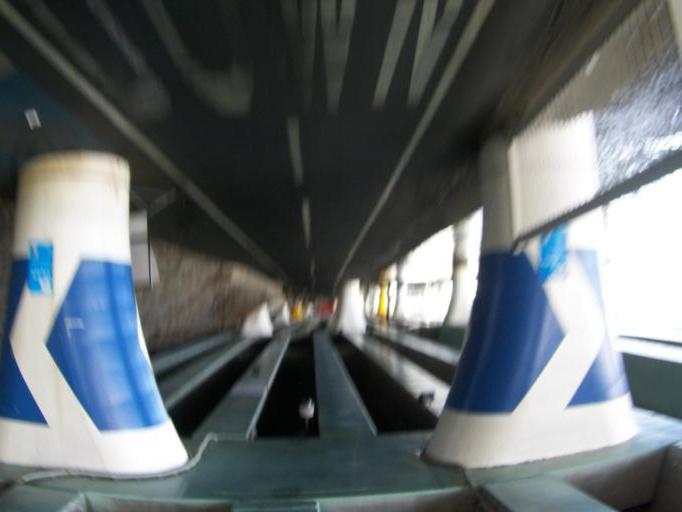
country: AU
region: Queensland
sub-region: Brisbane
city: Brisbane
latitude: -27.4718
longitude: 153.0224
